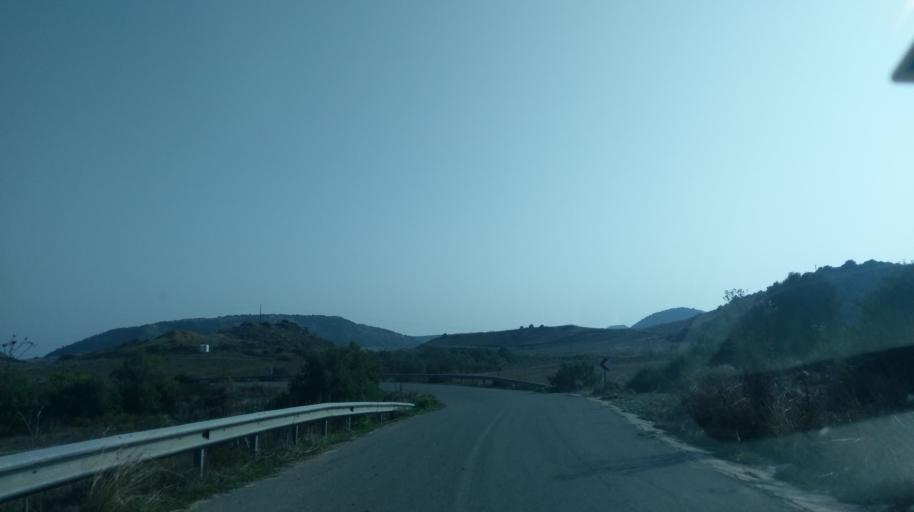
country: CY
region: Ammochostos
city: Rizokarpaso
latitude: 35.5122
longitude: 34.2803
